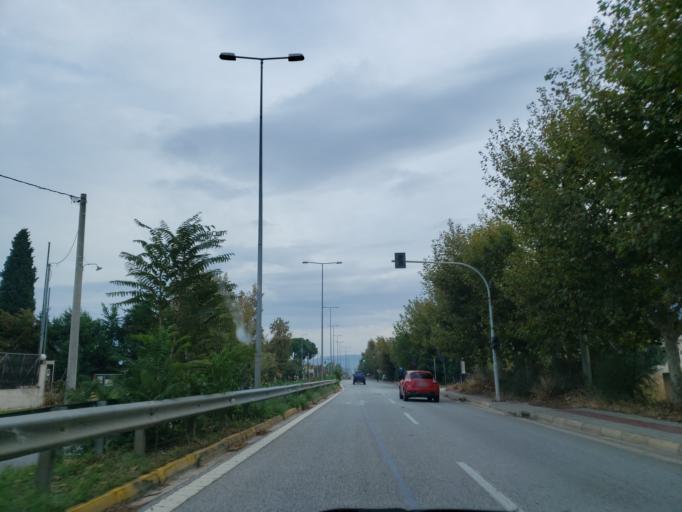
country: GR
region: Attica
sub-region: Nomarchia Anatolikis Attikis
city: Aghios Panteleimon
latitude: 38.1178
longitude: 23.9697
